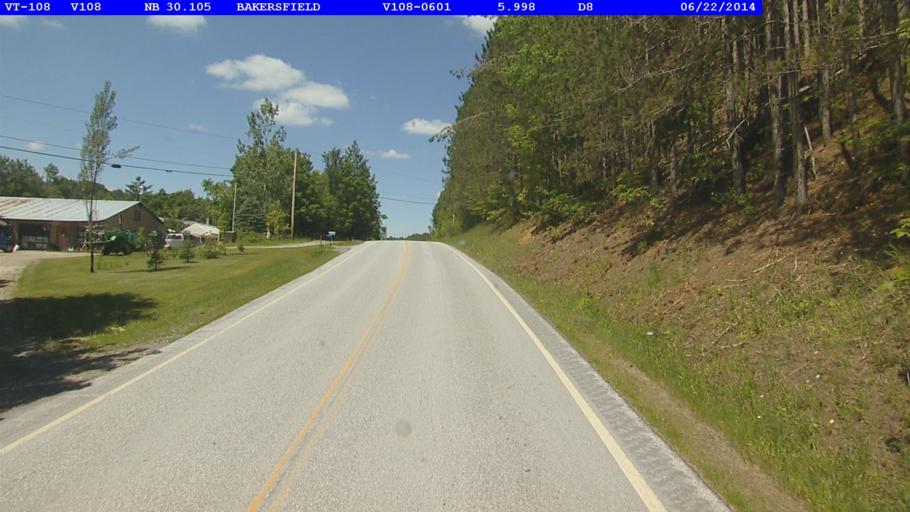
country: US
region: Vermont
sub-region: Franklin County
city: Enosburg Falls
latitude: 44.8127
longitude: -72.7901
